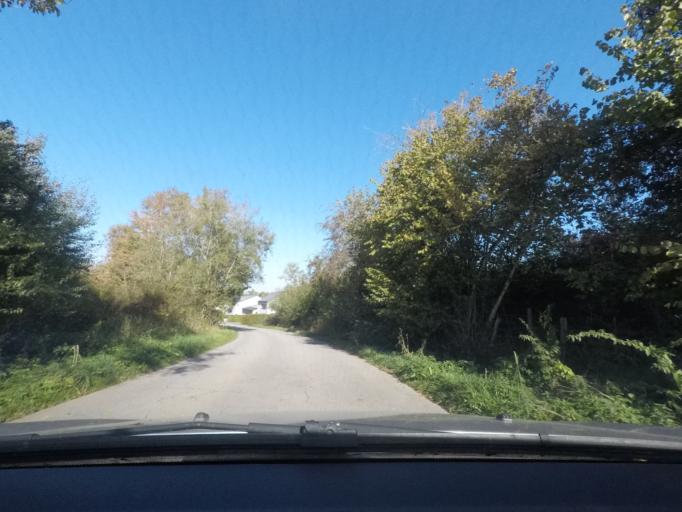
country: BE
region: Wallonia
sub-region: Province du Luxembourg
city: Habay-la-Vieille
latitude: 49.7170
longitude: 5.5661
